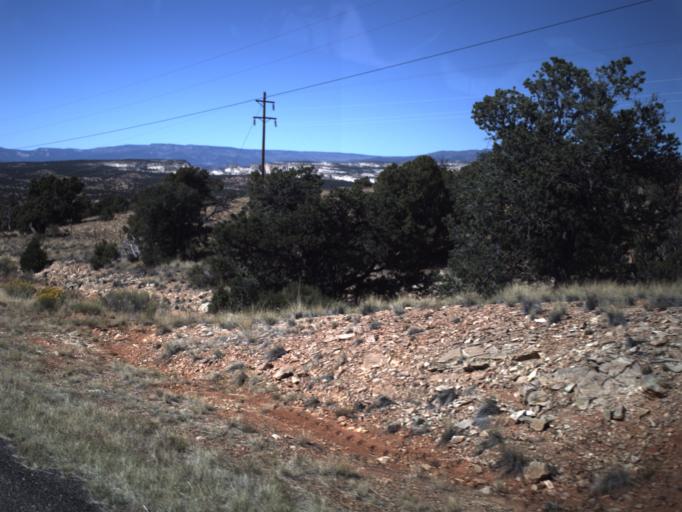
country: US
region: Utah
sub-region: Wayne County
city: Loa
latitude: 37.7501
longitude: -111.4742
